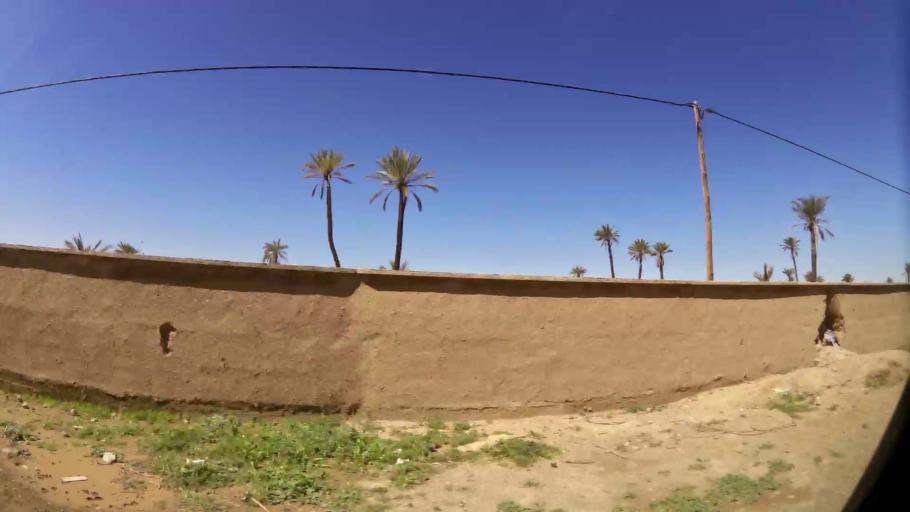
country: MA
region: Marrakech-Tensift-Al Haouz
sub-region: Marrakech
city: Marrakesh
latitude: 31.6720
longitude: -7.9800
